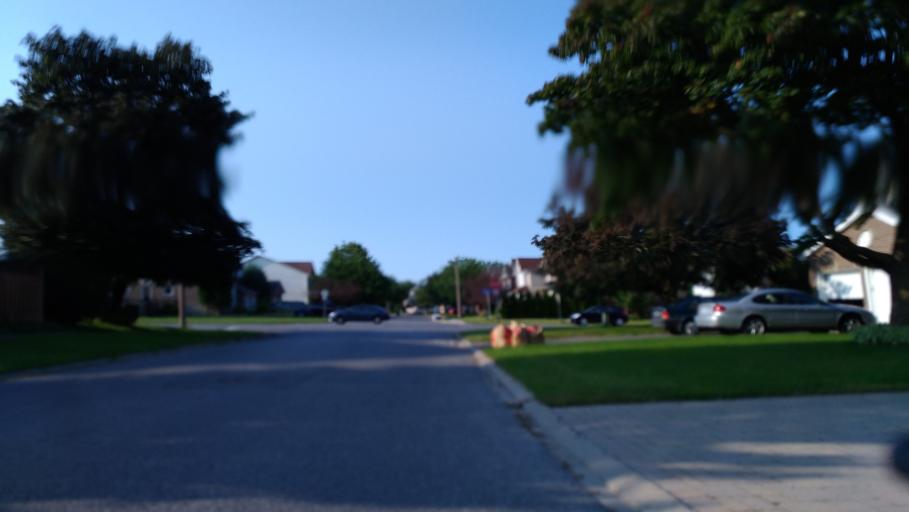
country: CA
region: Ontario
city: Bells Corners
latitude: 45.3495
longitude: -75.9296
